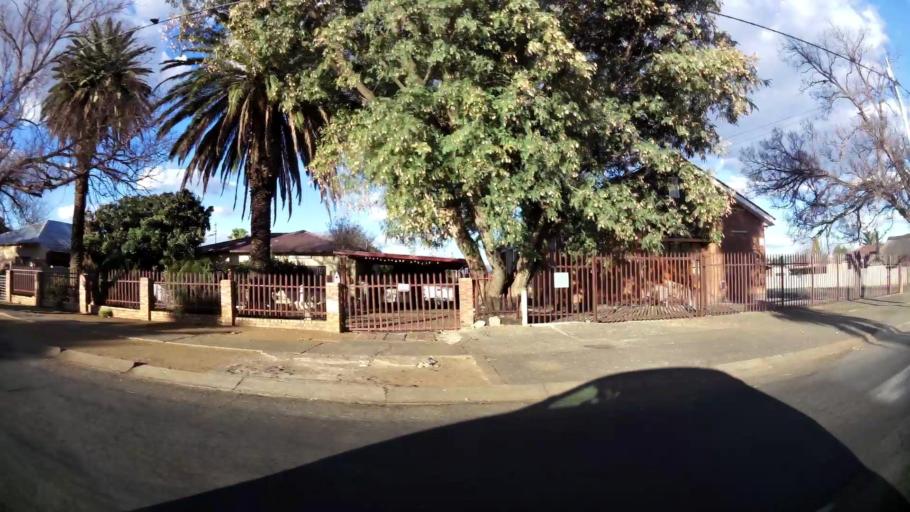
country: ZA
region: North-West
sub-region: Dr Kenneth Kaunda District Municipality
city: Potchefstroom
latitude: -26.7285
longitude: 27.0897
